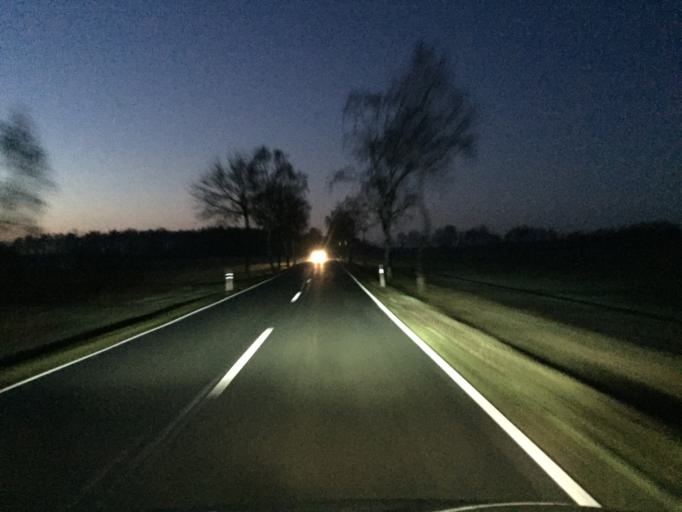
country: DE
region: Lower Saxony
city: Maasen
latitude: 52.6518
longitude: 8.8844
